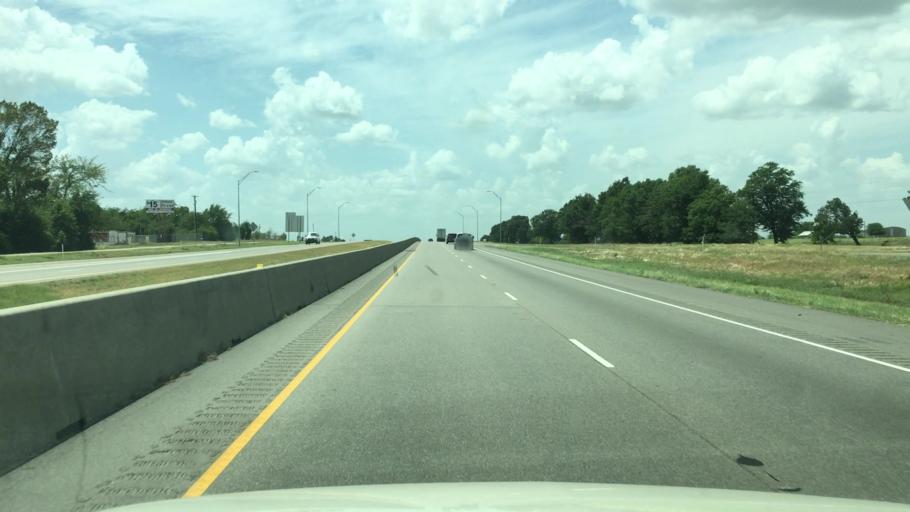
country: US
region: Texas
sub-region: Franklin County
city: Mount Vernon
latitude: 33.1623
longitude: -95.2404
